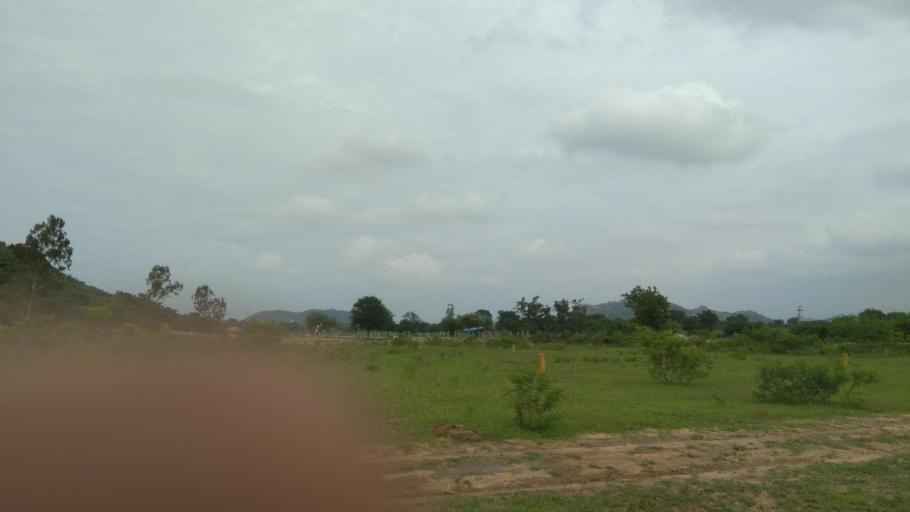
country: IN
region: Telangana
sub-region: Mahbubnagar
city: Farrukhnagar
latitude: 16.8862
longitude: 78.5142
